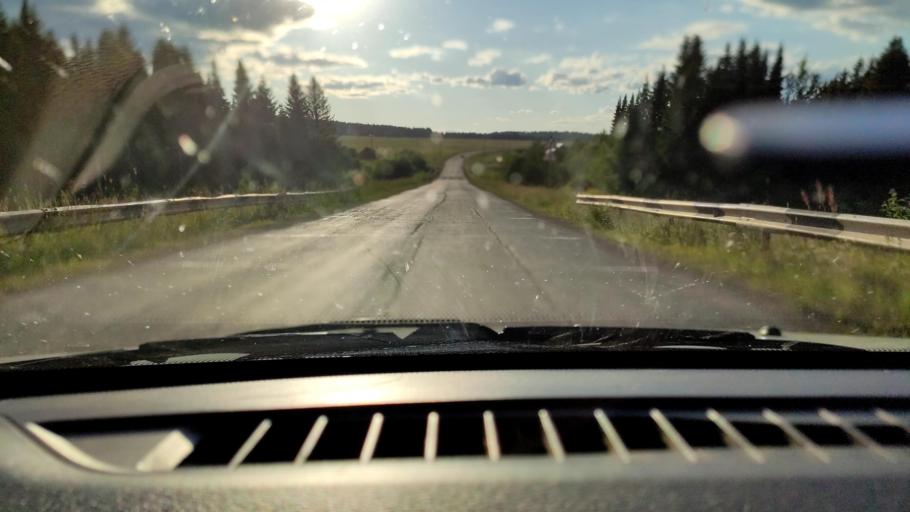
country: RU
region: Perm
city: Uinskoye
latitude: 57.0720
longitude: 56.5656
